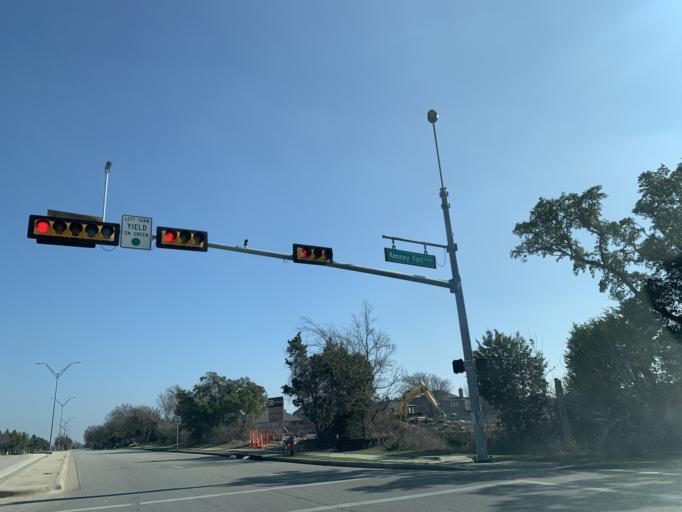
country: US
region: Texas
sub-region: Williamson County
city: Round Rock
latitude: 30.5087
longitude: -97.6363
